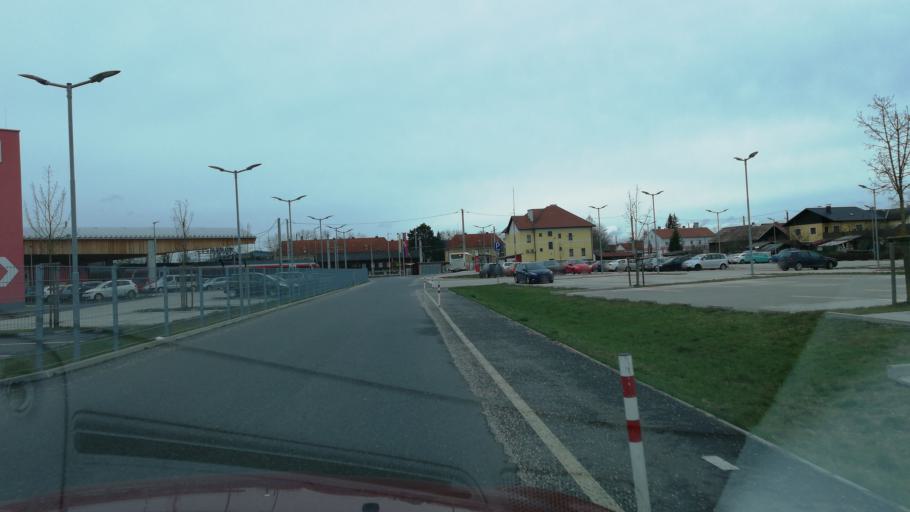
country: AT
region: Upper Austria
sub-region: Politischer Bezirk Urfahr-Umgebung
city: Feldkirchen an der Donau
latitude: 48.3019
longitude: 14.0173
